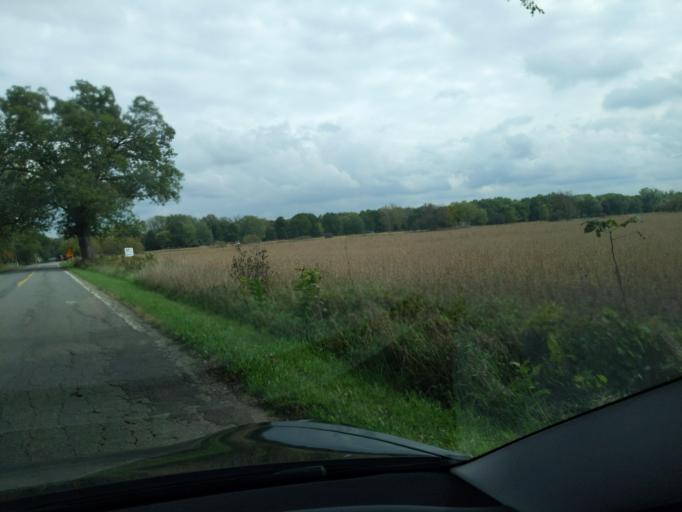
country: US
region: Michigan
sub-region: Ingham County
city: Leslie
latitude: 42.4115
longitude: -84.4473
